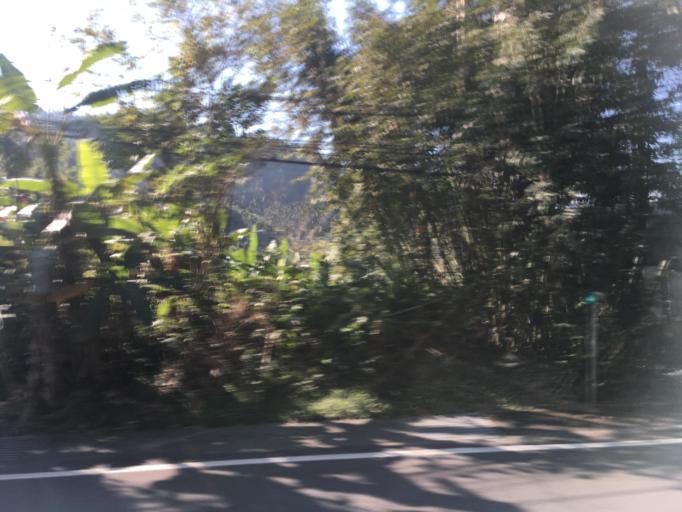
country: TW
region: Taiwan
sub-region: Chiayi
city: Jiayi Shi
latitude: 23.4217
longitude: 120.6434
